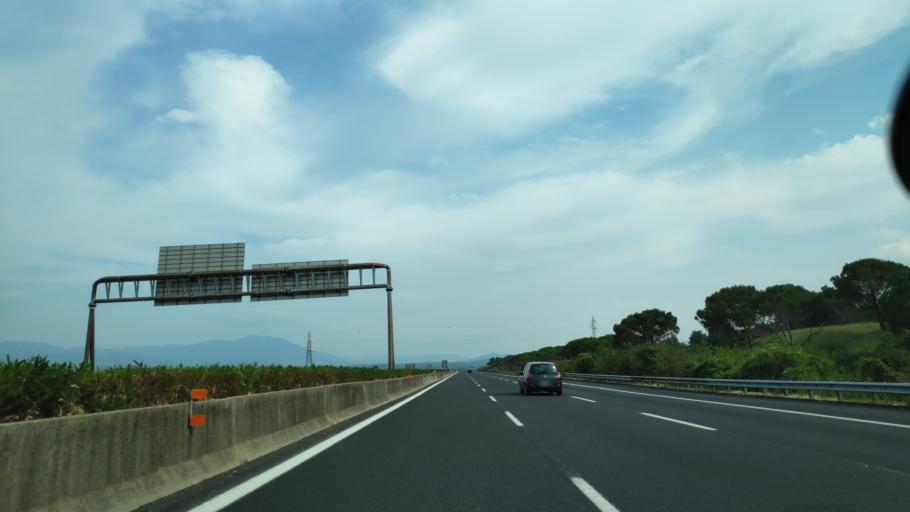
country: IT
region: Latium
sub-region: Citta metropolitana di Roma Capitale
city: Fiano Romano
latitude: 42.1649
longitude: 12.6164
